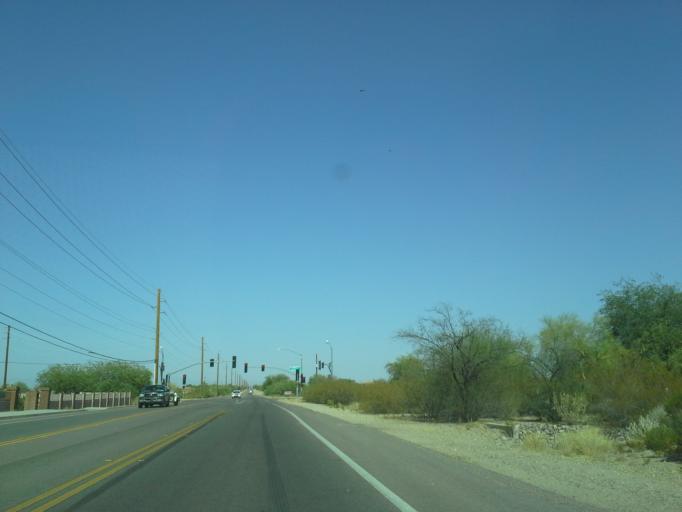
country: US
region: Arizona
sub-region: Maricopa County
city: Queen Creek
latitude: 33.2049
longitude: -111.6530
